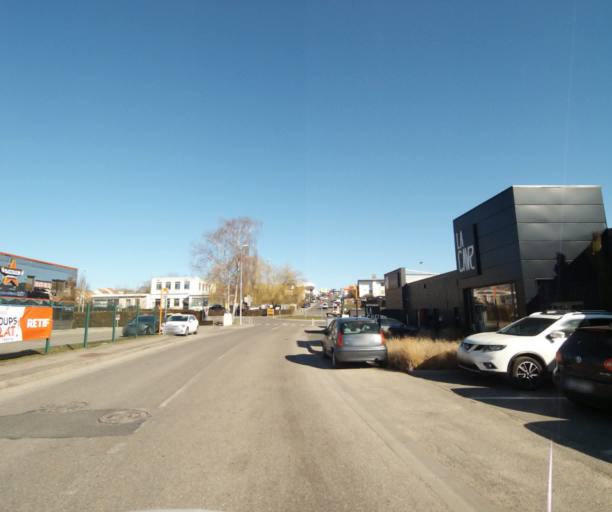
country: FR
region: Lorraine
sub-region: Departement de Meurthe-et-Moselle
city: Ludres
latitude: 48.6177
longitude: 6.1777
